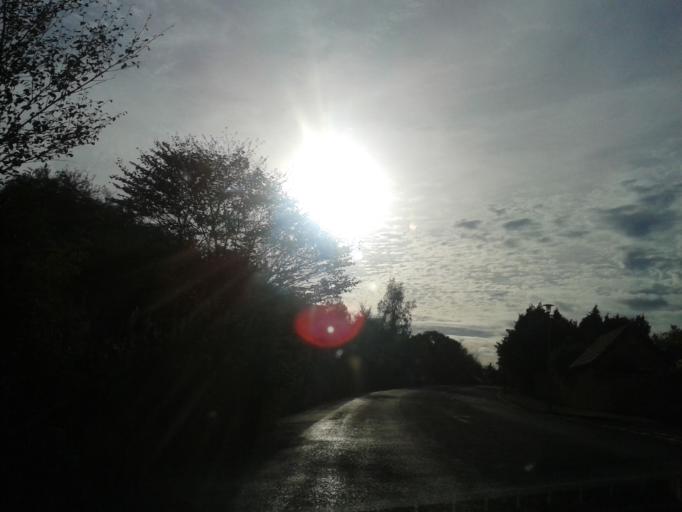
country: GB
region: Scotland
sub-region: Edinburgh
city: Edinburgh
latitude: 55.9176
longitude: -3.2033
